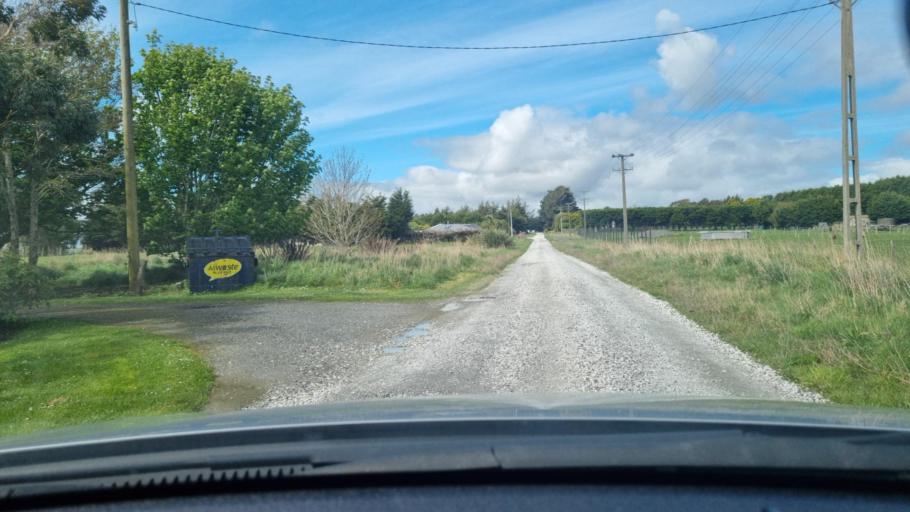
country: NZ
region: Southland
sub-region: Invercargill City
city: Invercargill
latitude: -46.4745
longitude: 168.3882
